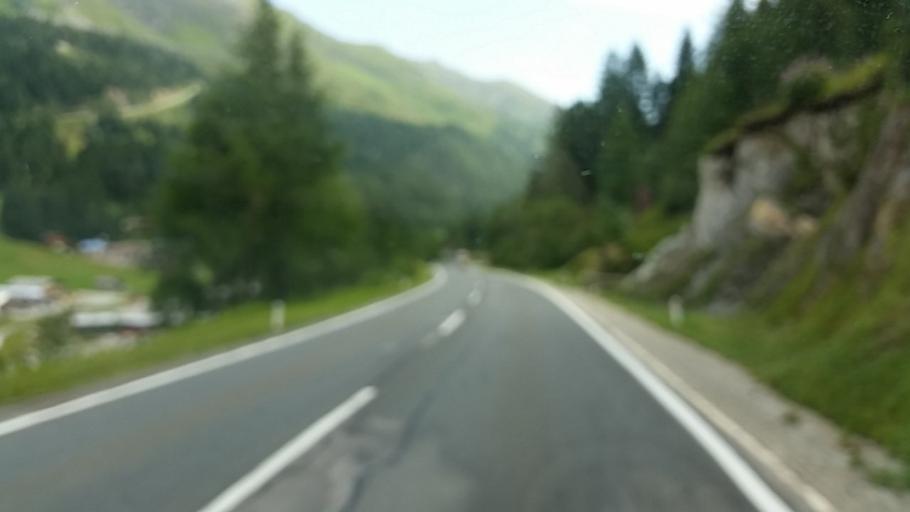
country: AT
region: Salzburg
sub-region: Politischer Bezirk Tamsweg
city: Tweng
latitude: 47.2420
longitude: 13.5678
